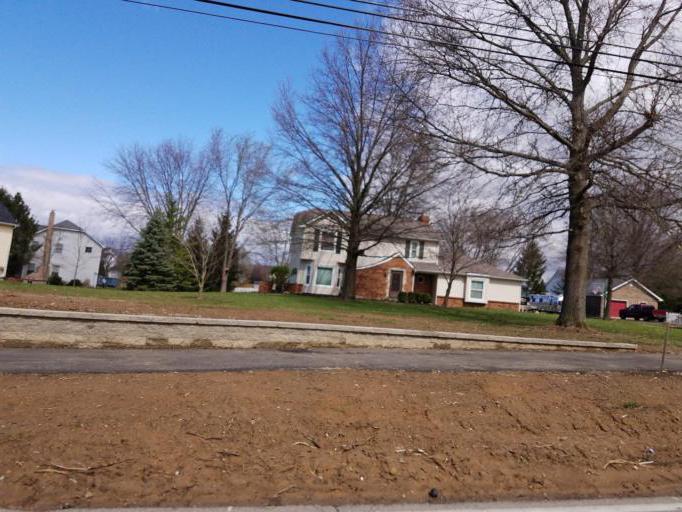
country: US
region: Ohio
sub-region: Franklin County
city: Westerville
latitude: 40.1452
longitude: -82.8874
